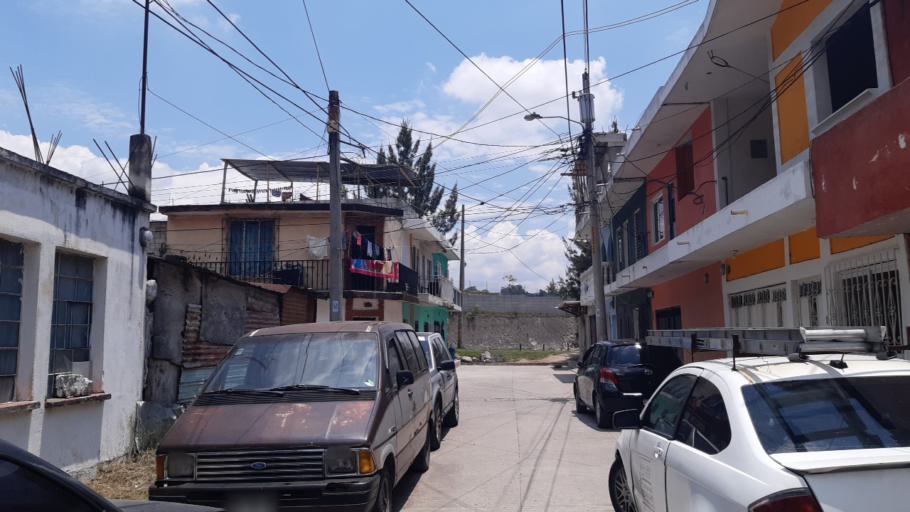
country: GT
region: Guatemala
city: Petapa
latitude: 14.5095
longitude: -90.5597
